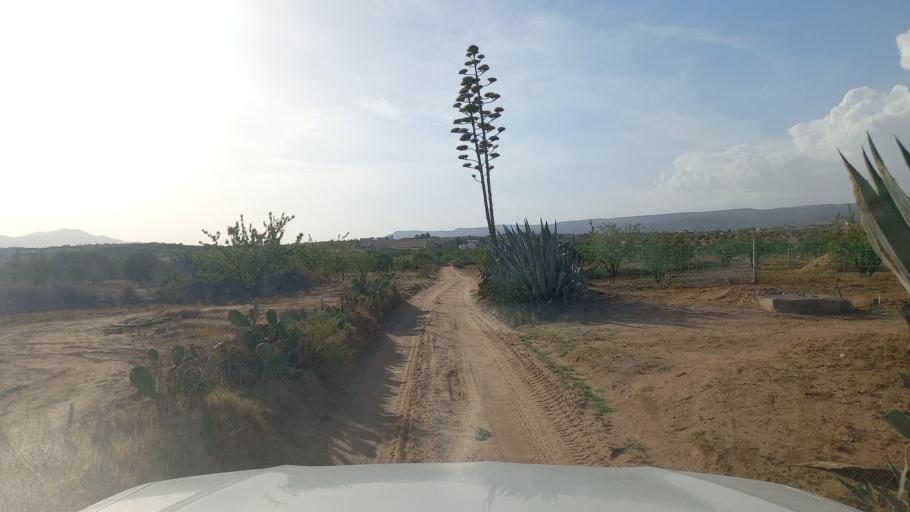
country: TN
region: Al Qasrayn
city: Kasserine
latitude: 35.2365
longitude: 8.9150
